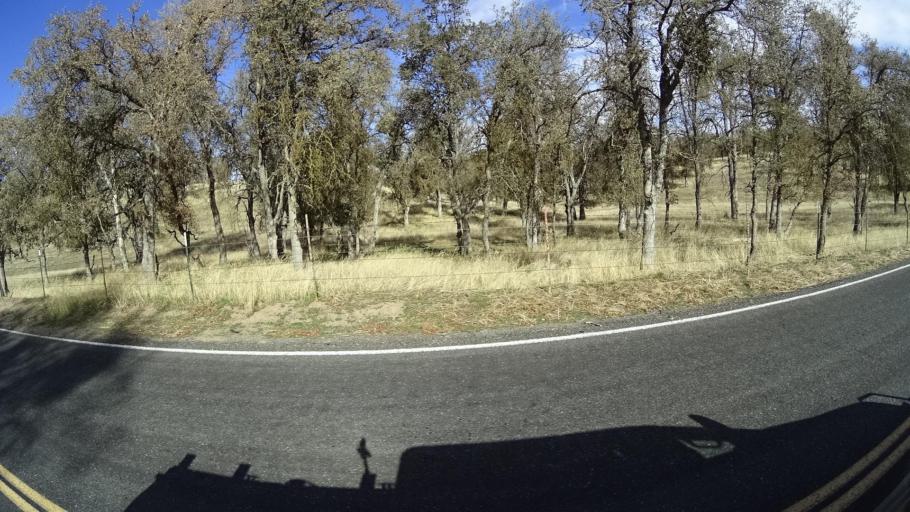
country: US
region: California
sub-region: Kern County
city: Alta Sierra
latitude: 35.6481
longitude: -118.7775
